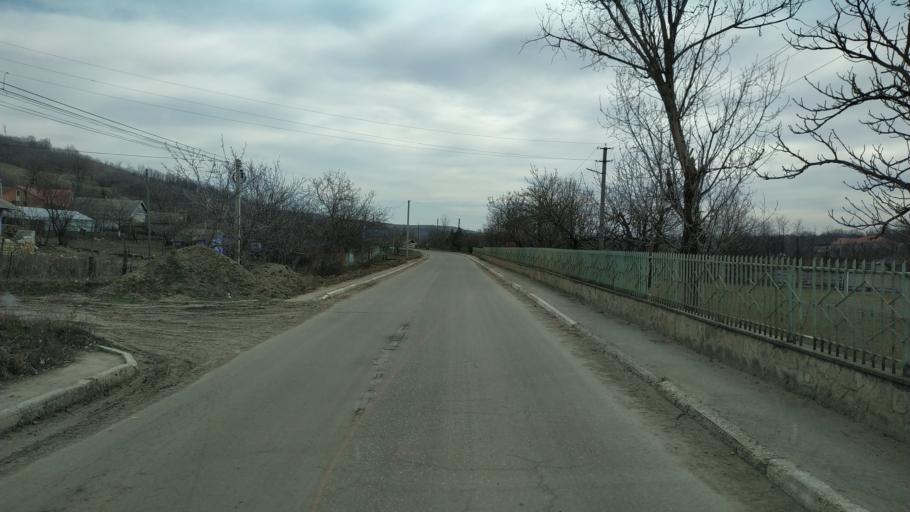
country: MD
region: Nisporeni
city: Nisporeni
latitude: 46.9660
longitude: 28.2144
